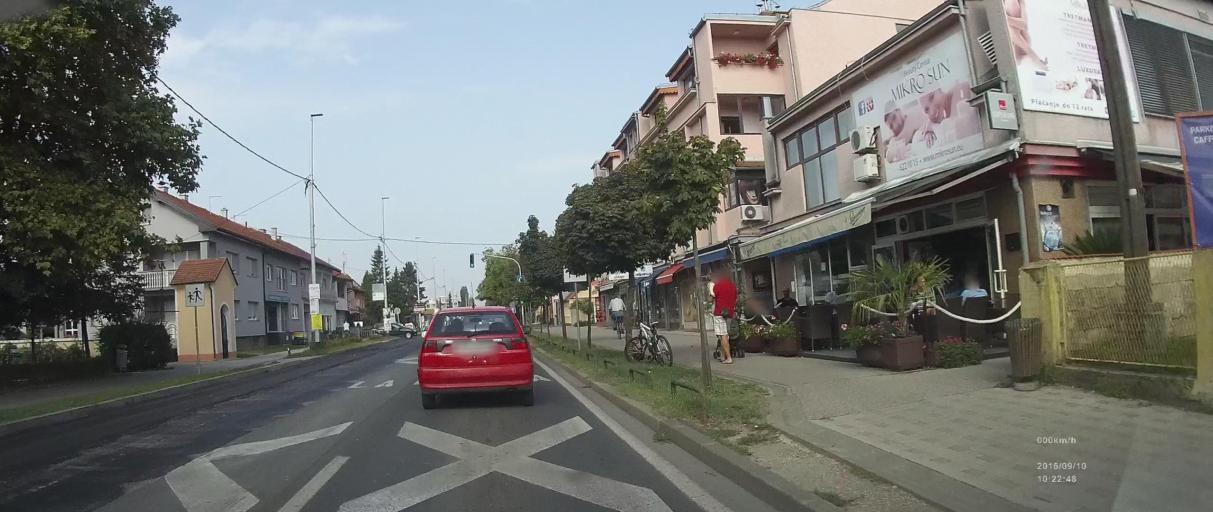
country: HR
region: Zagrebacka
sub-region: Grad Velika Gorica
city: Velika Gorica
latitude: 45.7164
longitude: 16.0695
